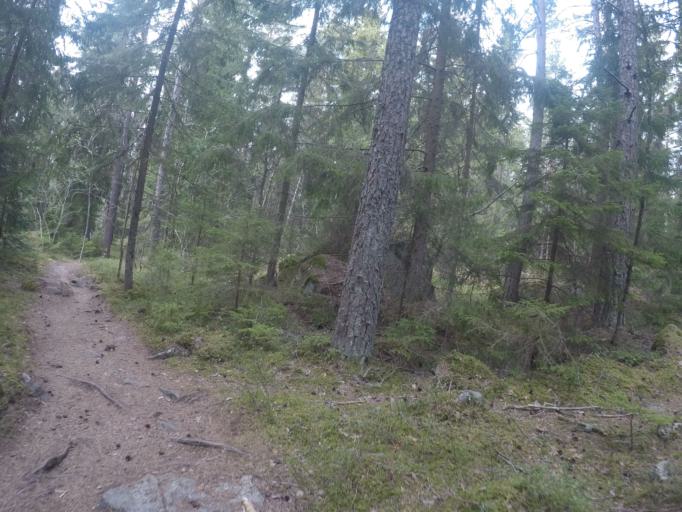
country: SE
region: Vaestmanland
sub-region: Vasteras
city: Vasteras
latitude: 59.6284
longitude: 16.5190
